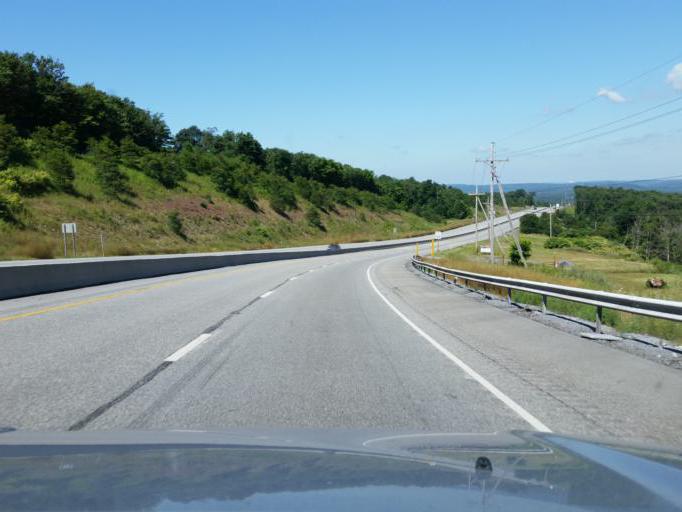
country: US
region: Pennsylvania
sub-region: Cambria County
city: Vinco
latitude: 40.4337
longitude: -78.9155
